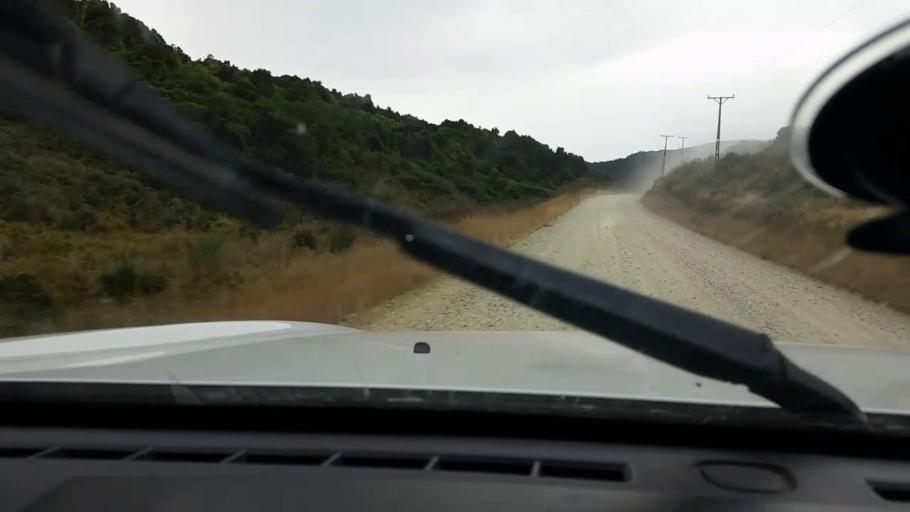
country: NZ
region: Otago
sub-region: Clutha District
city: Papatowai
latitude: -46.4670
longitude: 169.1284
